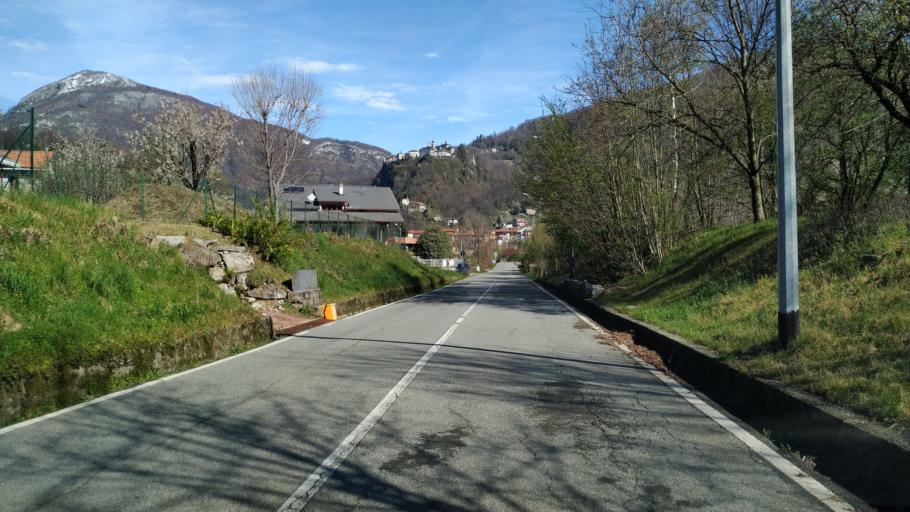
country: IT
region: Piedmont
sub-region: Provincia di Vercelli
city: Varallo
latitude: 45.8074
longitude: 8.2588
